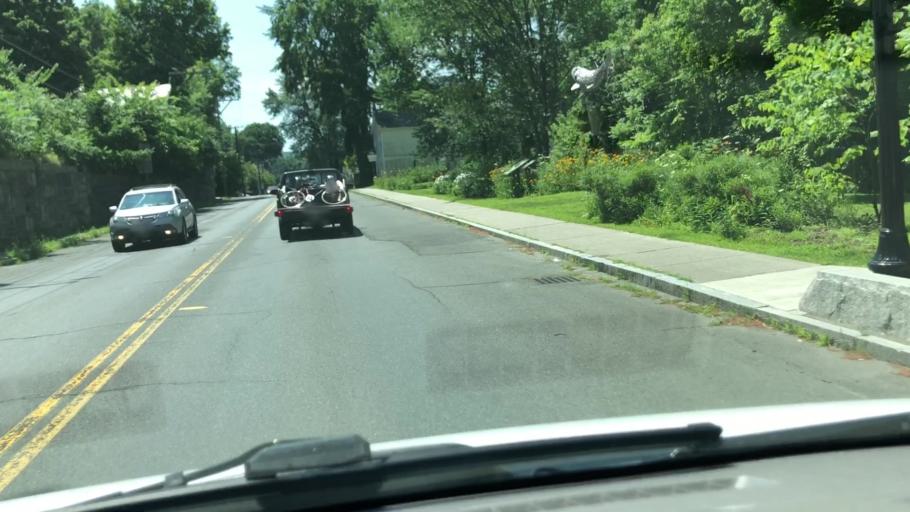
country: US
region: Massachusetts
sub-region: Franklin County
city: Greenfield
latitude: 42.5788
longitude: -72.5985
